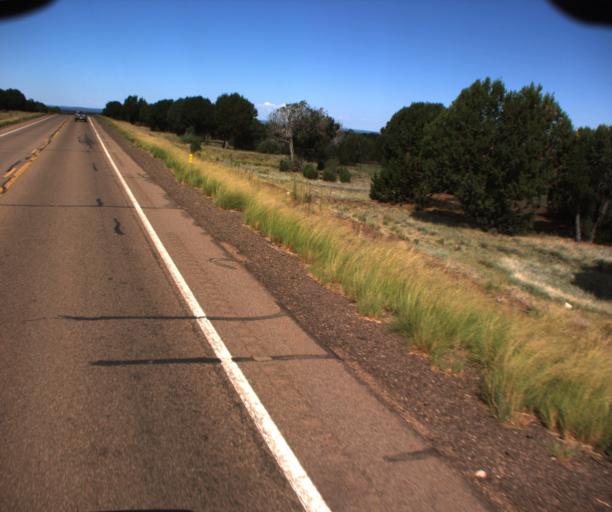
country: US
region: Arizona
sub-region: Navajo County
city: White Mountain Lake
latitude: 34.2738
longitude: -109.9066
